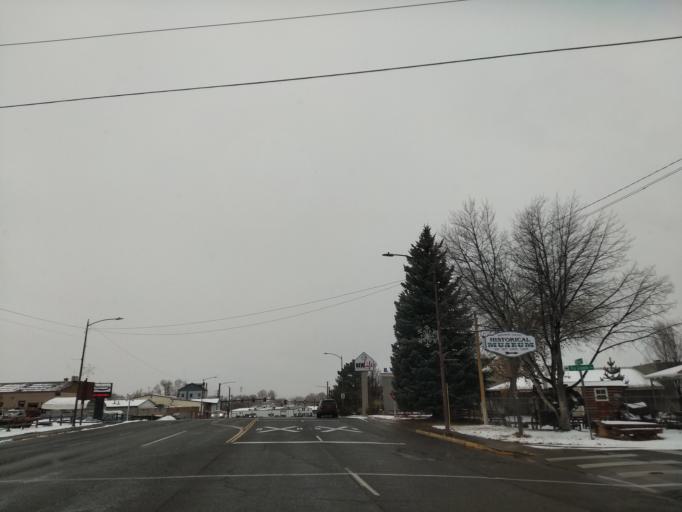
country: US
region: Colorado
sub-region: Montrose County
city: Montrose
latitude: 38.4778
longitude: -107.8793
